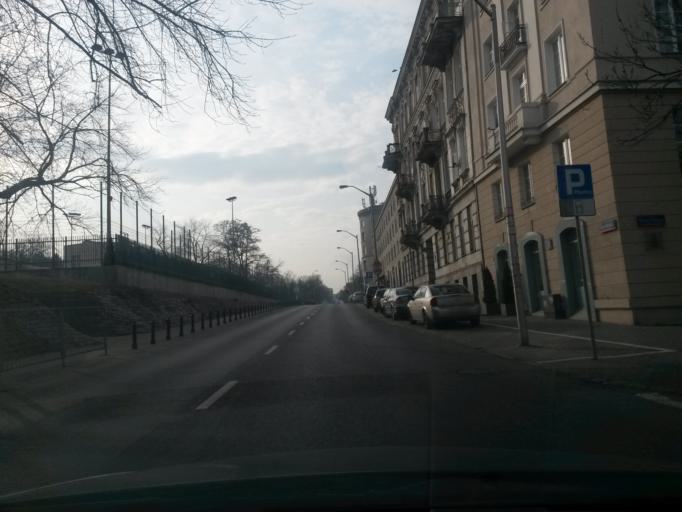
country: PL
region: Masovian Voivodeship
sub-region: Warszawa
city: Srodmiescie
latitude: 52.2244
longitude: 21.0301
